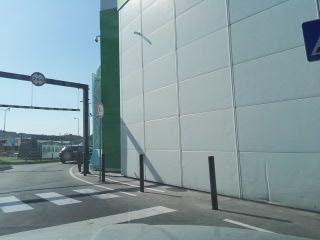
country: PT
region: Lisbon
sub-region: Oeiras
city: Alges
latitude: 38.7260
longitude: -9.2157
